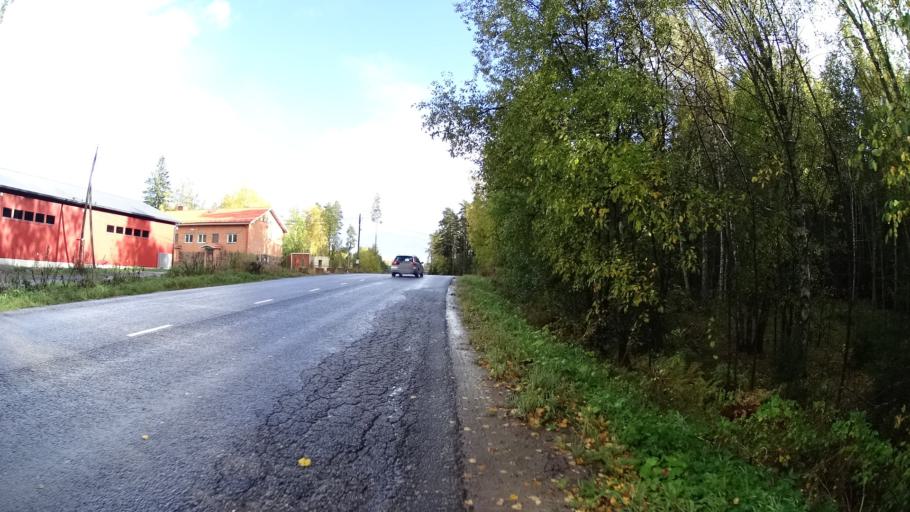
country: FI
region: Uusimaa
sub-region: Helsinki
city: Kilo
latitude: 60.2869
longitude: 24.8114
